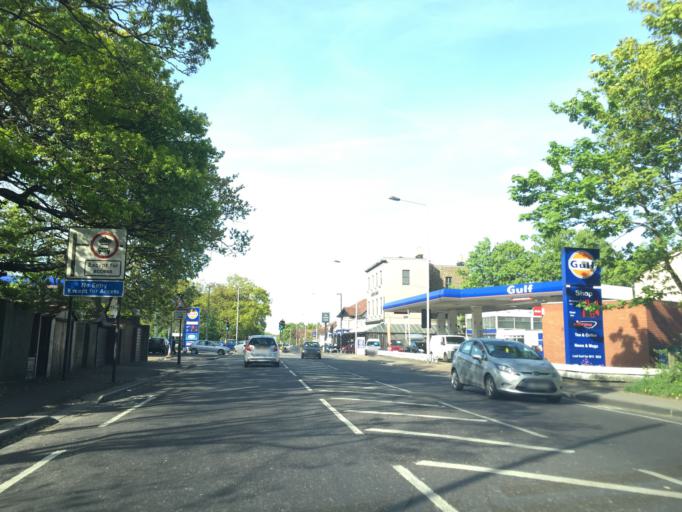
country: GB
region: England
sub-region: Greater London
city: Woodford Green
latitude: 51.5998
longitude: 0.0131
